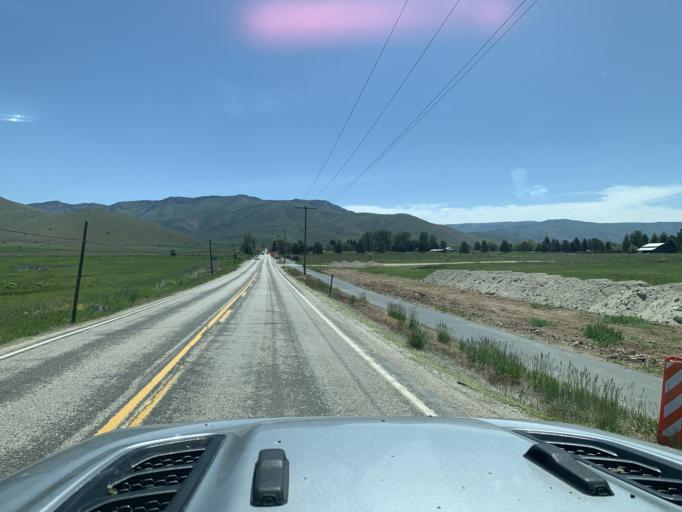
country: US
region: Utah
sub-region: Weber County
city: Wolf Creek
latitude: 41.2932
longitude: -111.7869
